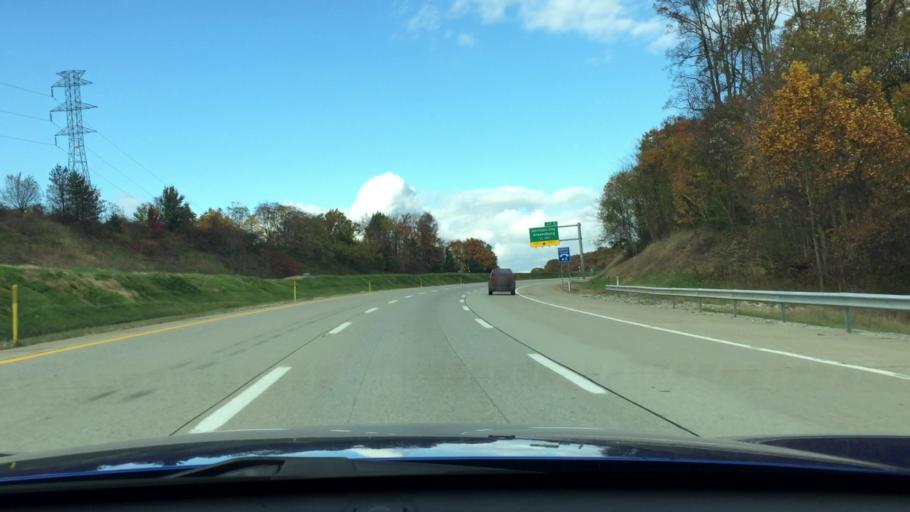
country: US
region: Pennsylvania
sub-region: Westmoreland County
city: Jeannette
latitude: 40.3357
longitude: -79.5808
